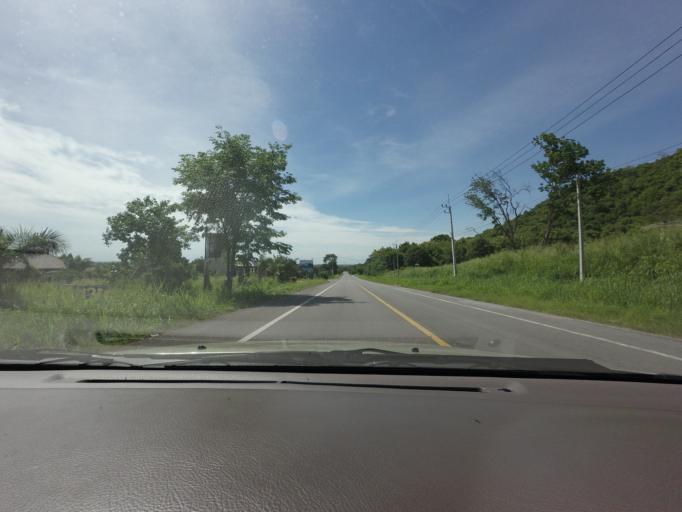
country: TH
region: Chon Buri
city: Si Racha
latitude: 13.2423
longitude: 100.9604
